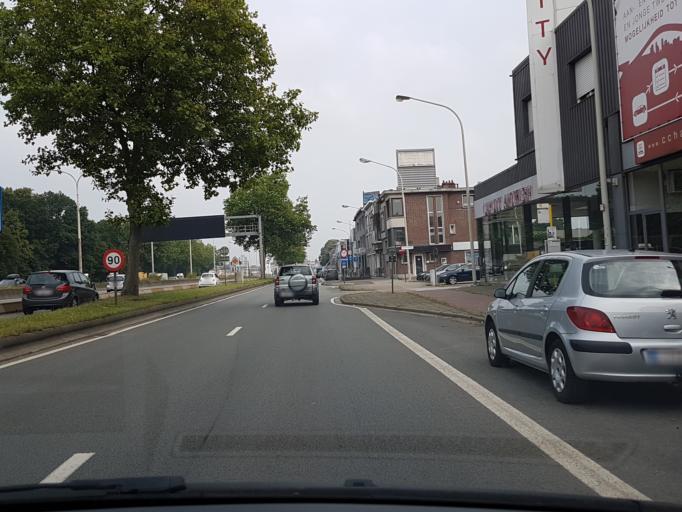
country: BE
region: Flanders
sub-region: Provincie Antwerpen
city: Hoboken
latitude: 51.1761
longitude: 4.3889
